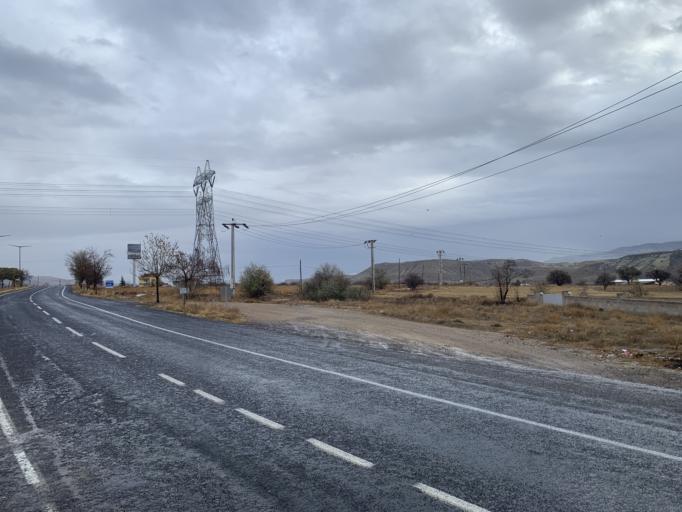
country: TR
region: Nevsehir
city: Avanos
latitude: 38.7220
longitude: 34.8632
